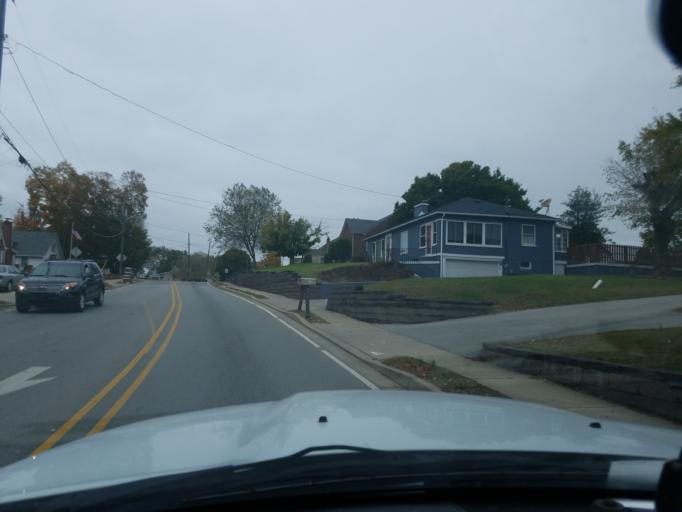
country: US
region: Indiana
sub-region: Floyd County
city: New Albany
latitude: 38.3071
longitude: -85.8222
